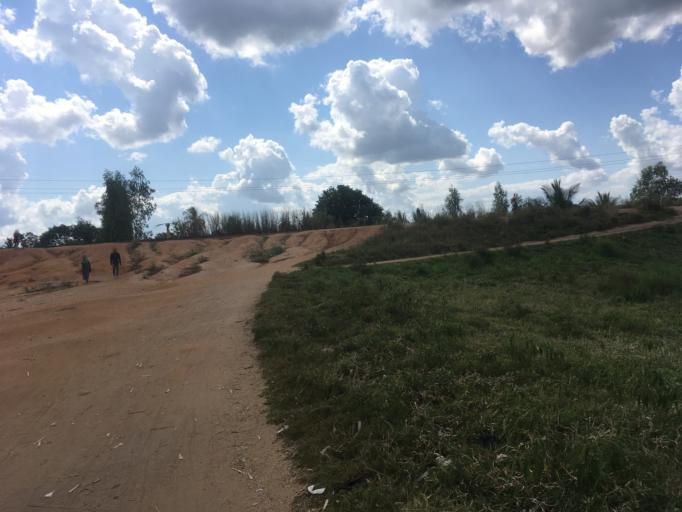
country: MZ
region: Zambezia
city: Quelimane
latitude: -17.5786
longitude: 36.6952
